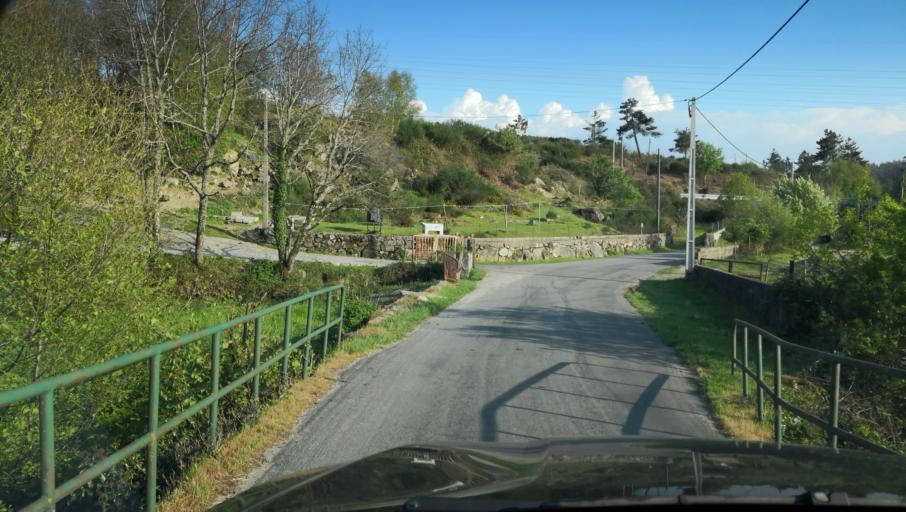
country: PT
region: Vila Real
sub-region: Santa Marta de Penaguiao
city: Santa Marta de Penaguiao
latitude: 41.2857
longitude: -7.8319
